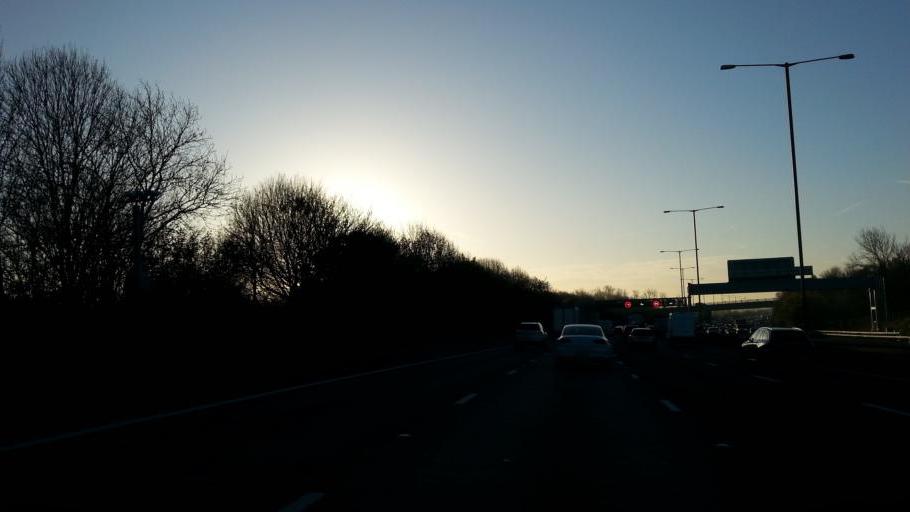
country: GB
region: England
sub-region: Greater London
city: Uxbridge
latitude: 51.5425
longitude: -0.5037
